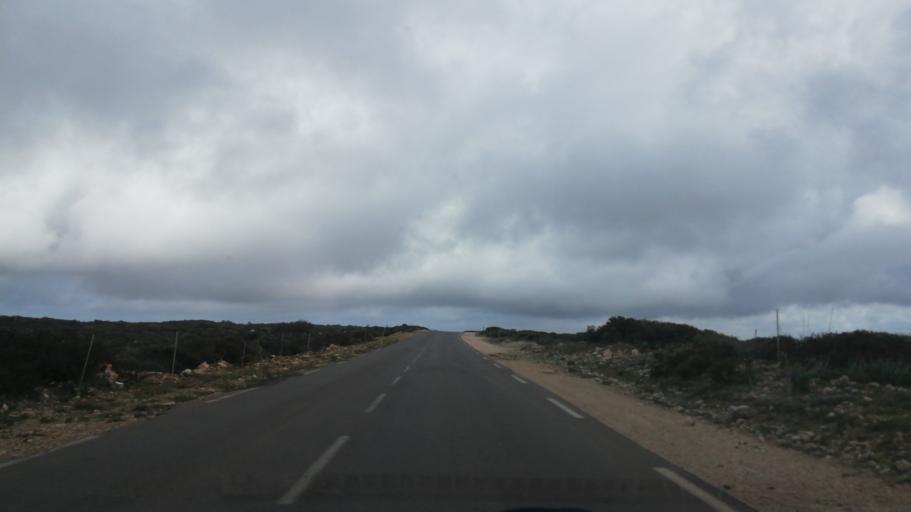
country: DZ
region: Oran
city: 'Ain el Turk
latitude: 35.6988
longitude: -0.7671
